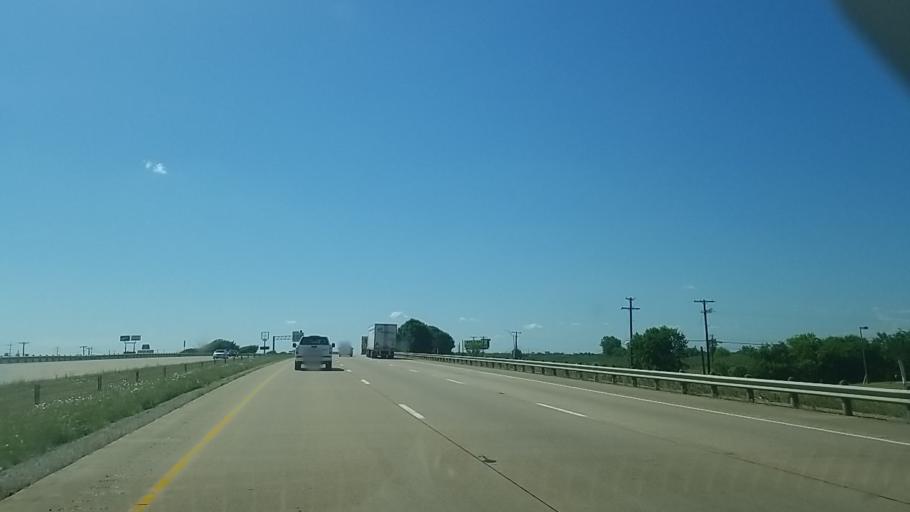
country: US
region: Texas
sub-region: Ellis County
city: Ennis
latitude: 32.3095
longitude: -96.5946
